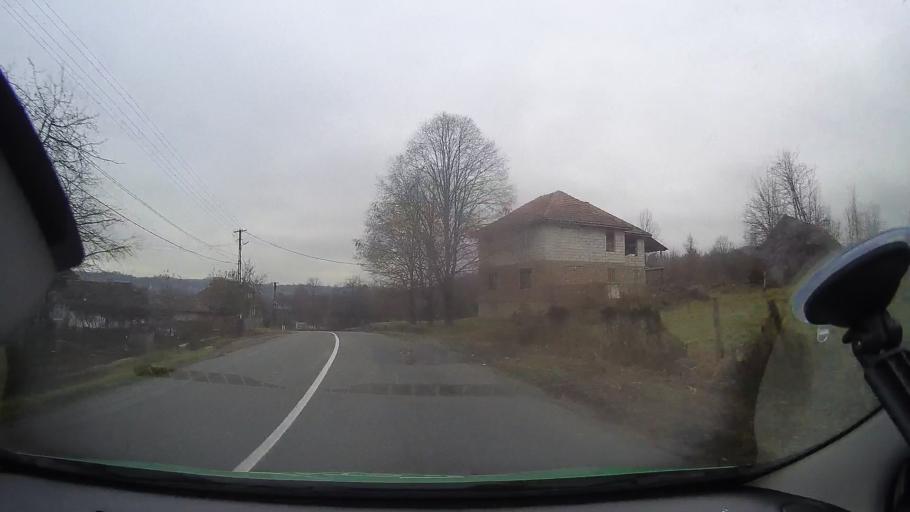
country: RO
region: Arad
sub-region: Comuna Varfurile
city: Varfurile
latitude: 46.3142
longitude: 22.5126
